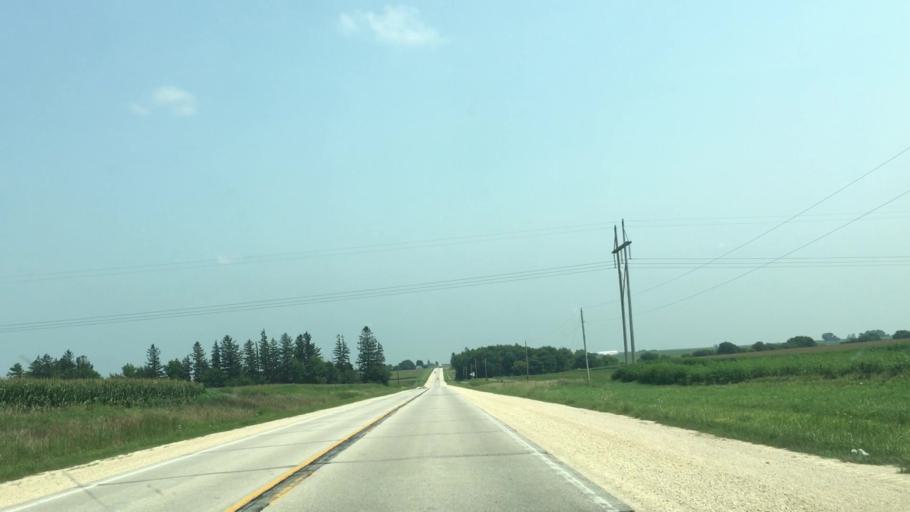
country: US
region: Iowa
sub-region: Fayette County
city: Oelwein
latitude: 42.6798
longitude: -91.8552
